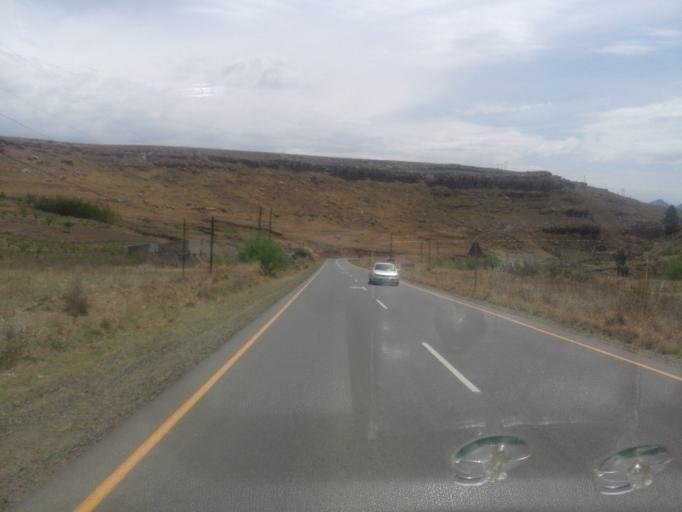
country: LS
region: Qacha's Nek
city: Qacha's Nek
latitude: -30.1060
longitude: 28.6596
